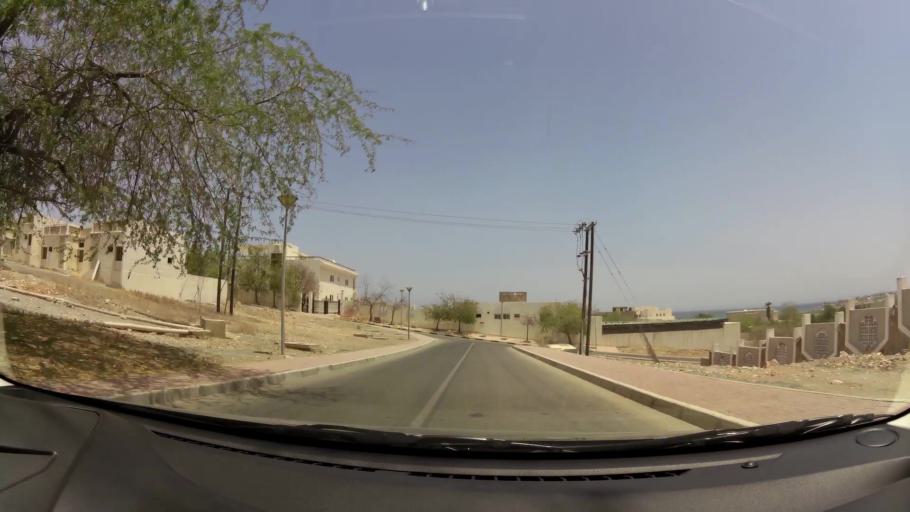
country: OM
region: Muhafazat Masqat
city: Bawshar
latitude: 23.6094
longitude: 58.4681
